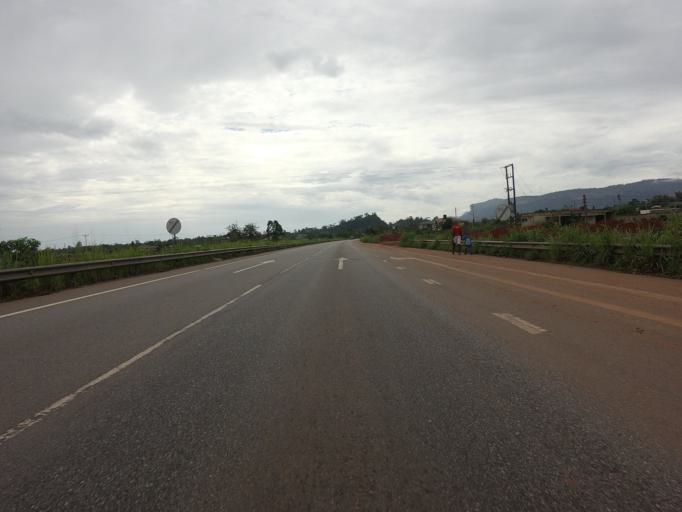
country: GH
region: Eastern
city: Nkawkaw
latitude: 6.5451
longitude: -0.7909
